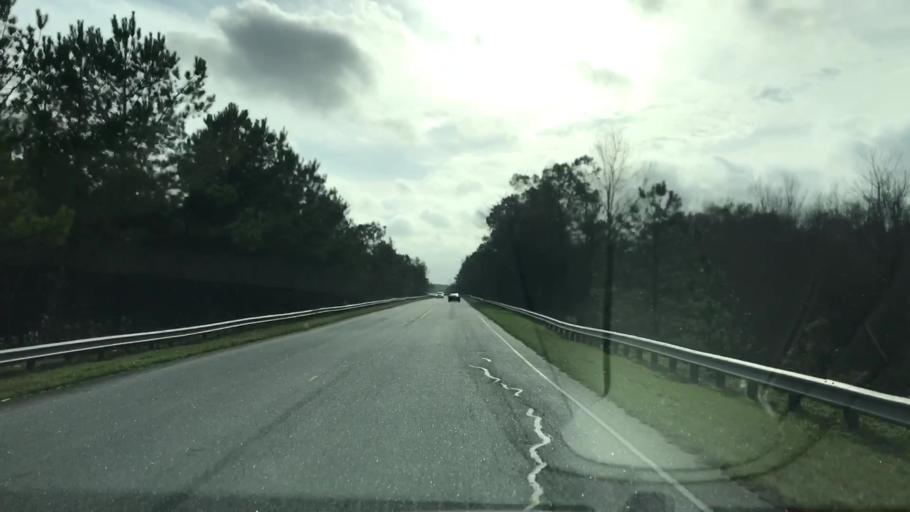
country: US
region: South Carolina
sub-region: Williamsburg County
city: Andrews
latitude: 33.3153
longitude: -79.6693
